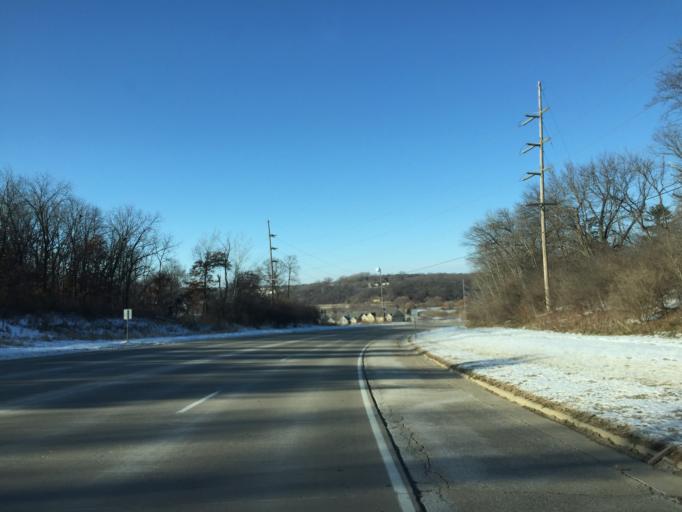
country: US
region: Minnesota
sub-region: Olmsted County
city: Rochester
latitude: 44.0139
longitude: -92.5156
